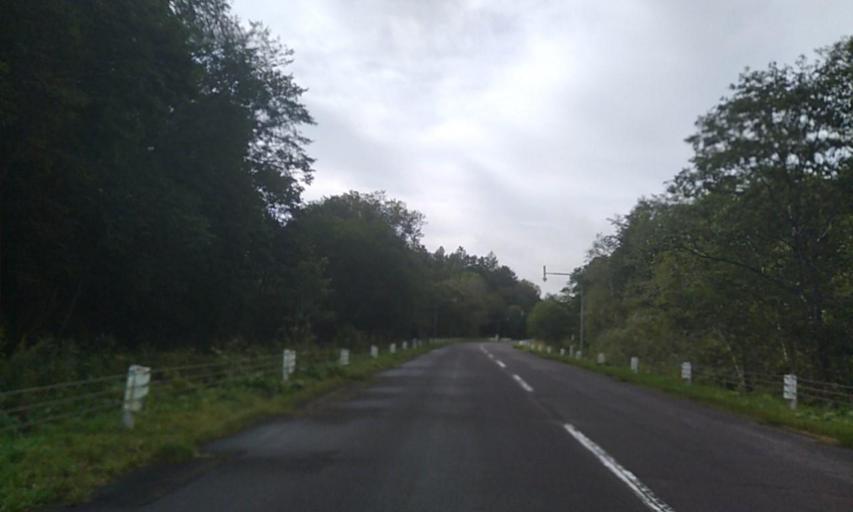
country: JP
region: Hokkaido
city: Abashiri
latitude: 43.6642
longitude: 144.5558
